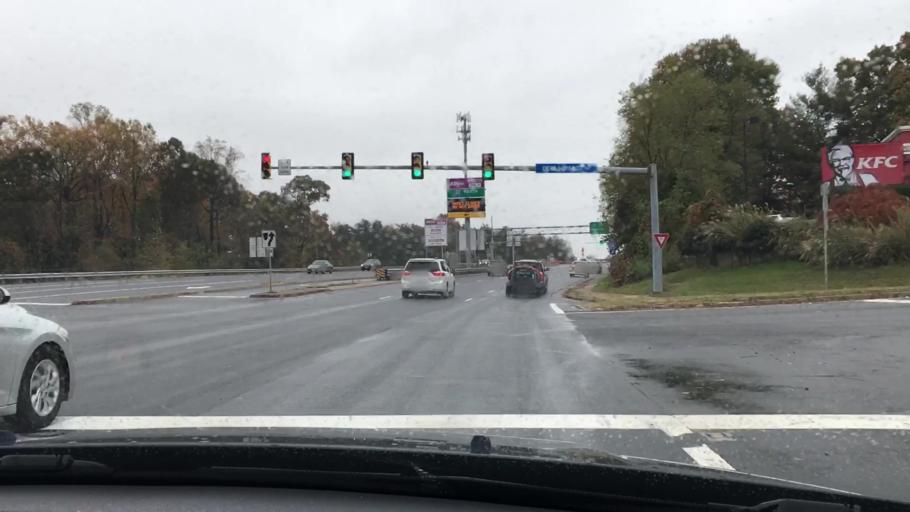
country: US
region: Virginia
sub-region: Prince William County
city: Woodbridge
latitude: 38.6742
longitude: -77.2546
